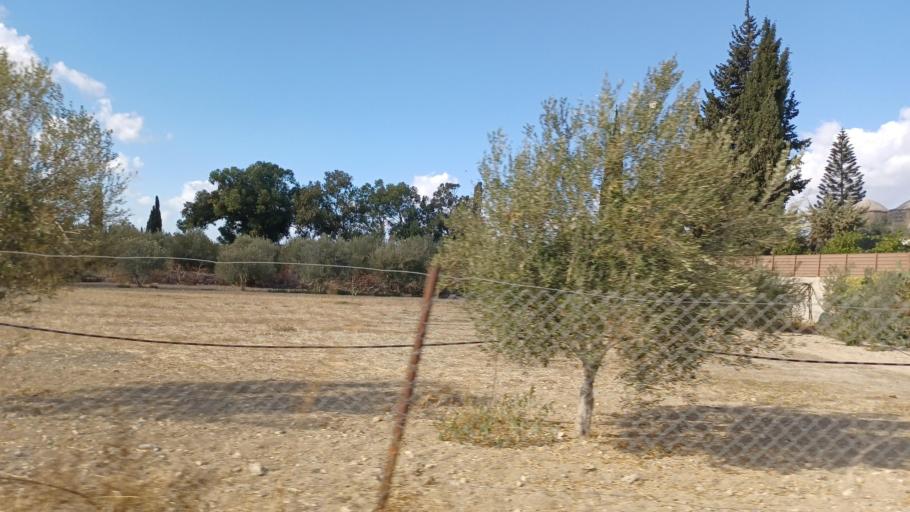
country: CY
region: Limassol
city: Pano Polemidia
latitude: 34.7006
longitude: 33.0004
